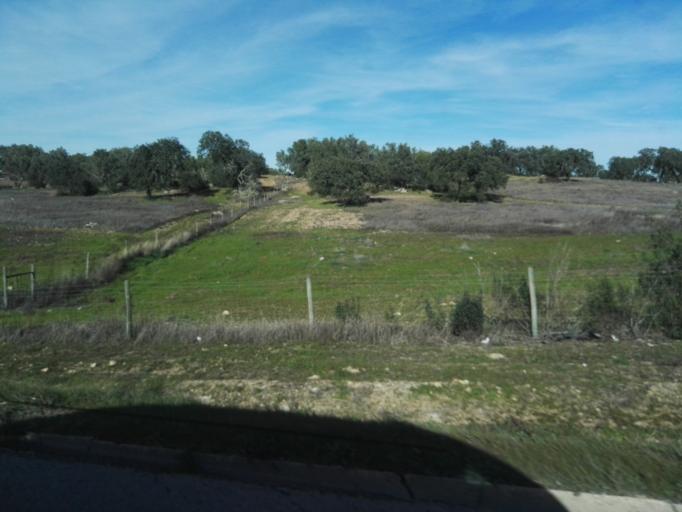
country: PT
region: Evora
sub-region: Arraiolos
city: Arraiolos
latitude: 38.8662
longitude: -7.9442
